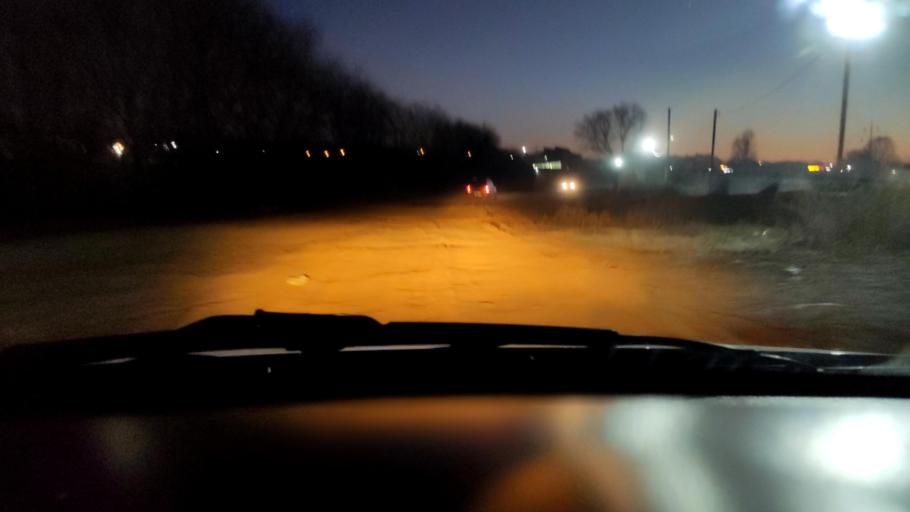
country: RU
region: Voronezj
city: Voronezh
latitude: 51.6717
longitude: 39.1309
